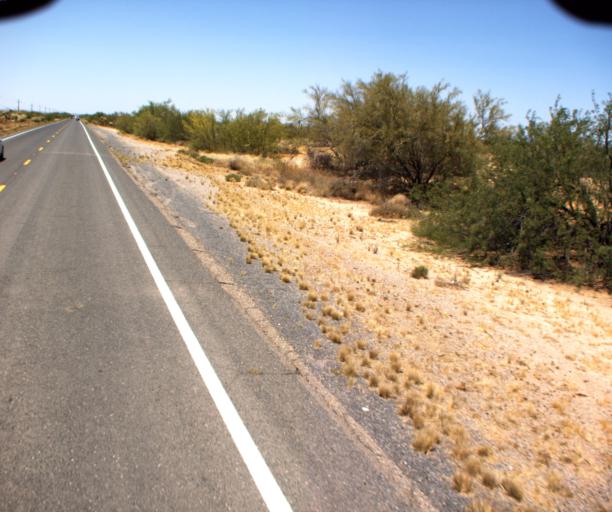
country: US
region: Arizona
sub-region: Pinal County
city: Florence
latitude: 32.9373
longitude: -111.3133
